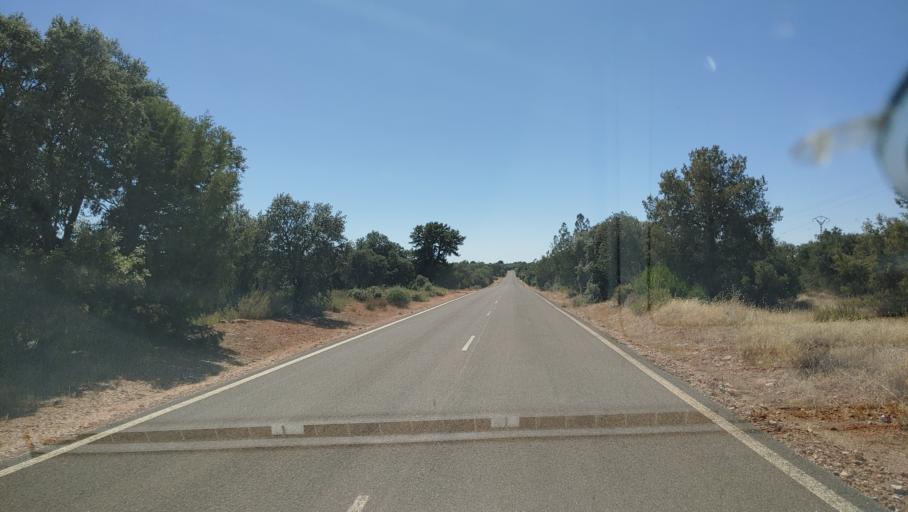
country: ES
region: Castille-La Mancha
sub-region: Provincia de Ciudad Real
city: Villahermosa
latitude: 38.8407
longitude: -2.8139
